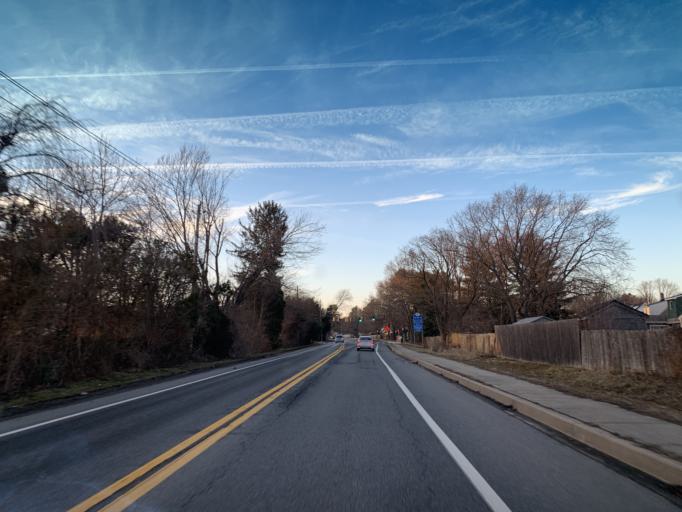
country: US
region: Delaware
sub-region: New Castle County
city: Bear
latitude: 39.6566
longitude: -75.6360
